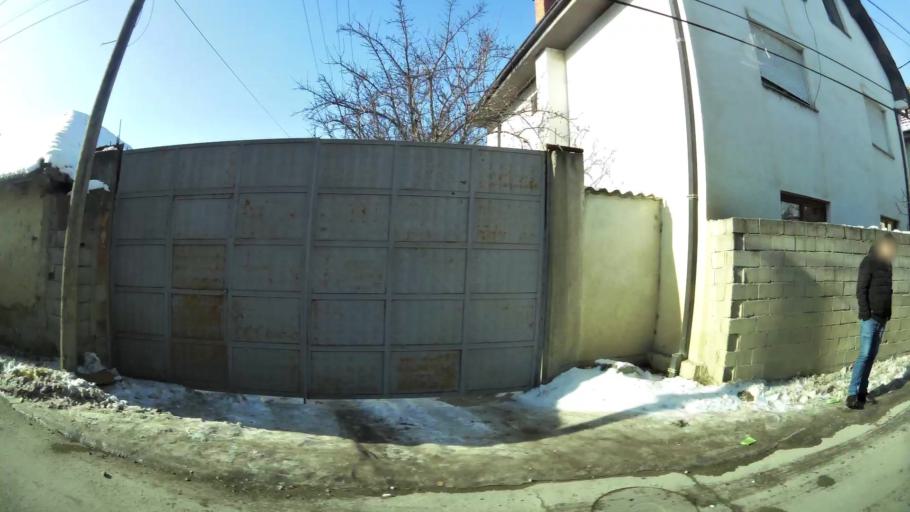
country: MK
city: Grchec
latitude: 41.9896
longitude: 21.3304
